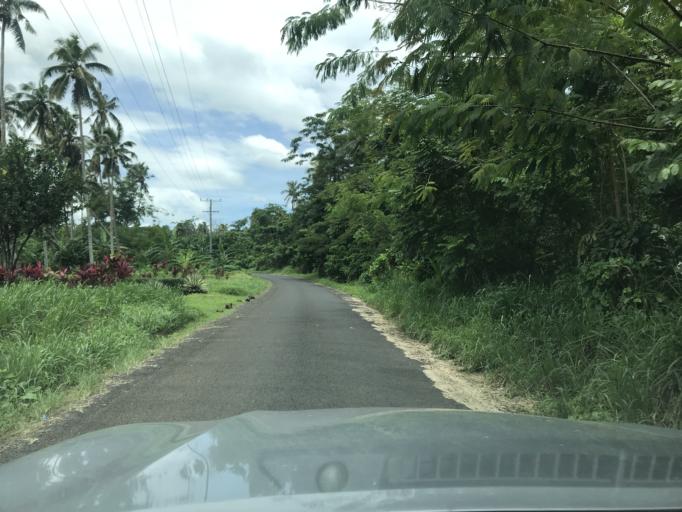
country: WS
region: Tuamasaga
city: Afenga
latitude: -13.8144
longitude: -171.8857
